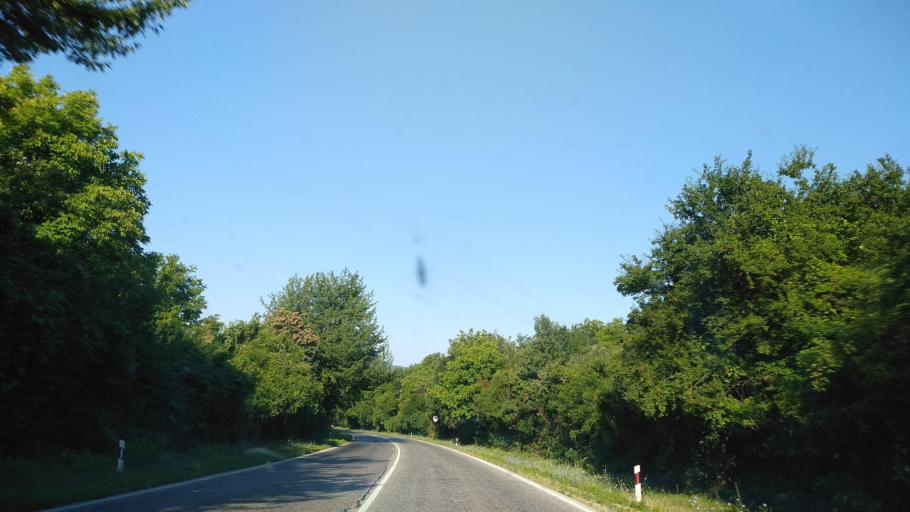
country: BG
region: Lovech
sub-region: Obshtina Lovech
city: Lovech
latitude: 43.0482
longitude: 24.7593
